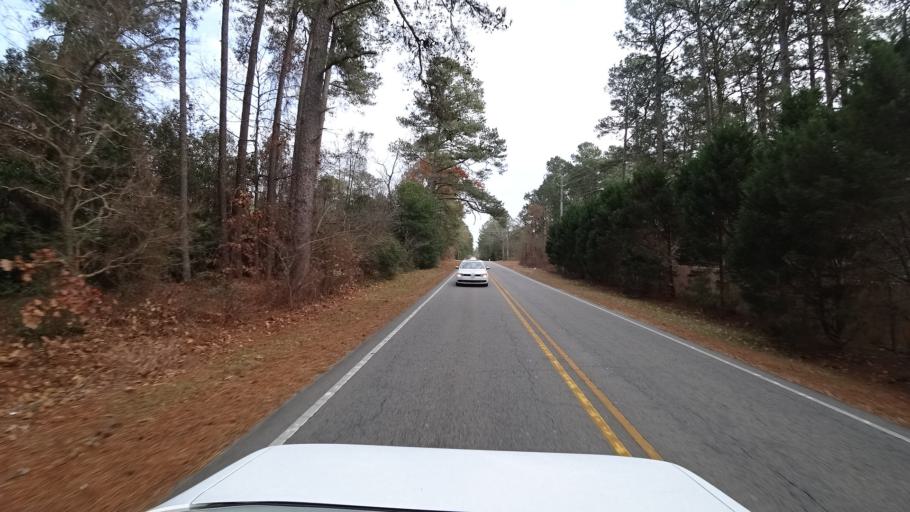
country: US
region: North Carolina
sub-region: Moore County
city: Pinehurst
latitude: 35.1818
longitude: -79.4558
